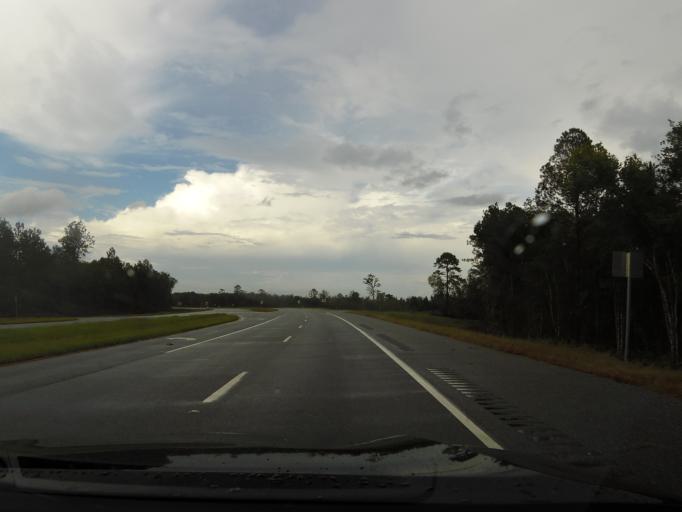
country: US
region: Georgia
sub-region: Wayne County
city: Jesup
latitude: 31.6077
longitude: -81.8598
